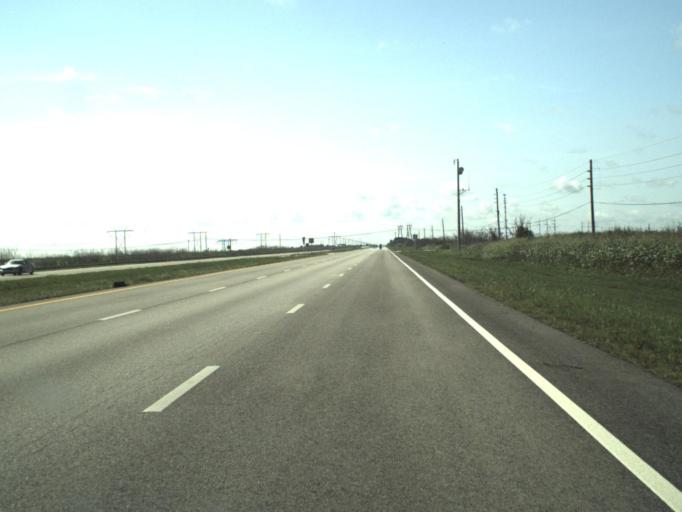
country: US
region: Florida
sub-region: Broward County
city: Coral Springs
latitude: 26.3503
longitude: -80.5500
